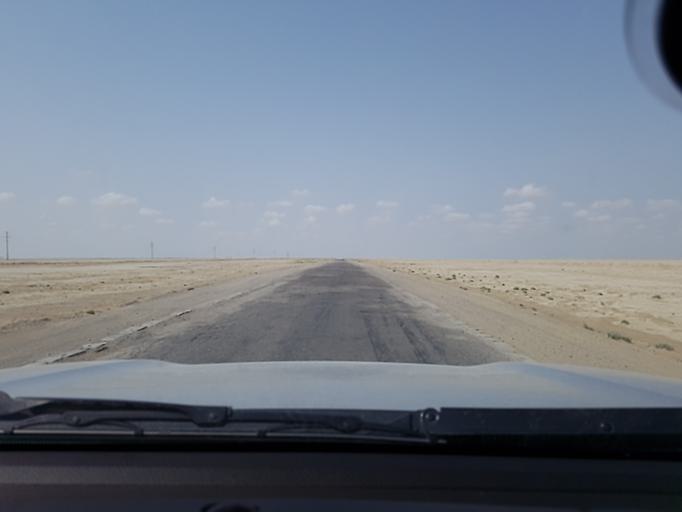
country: TM
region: Balkan
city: Gumdag
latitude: 38.6440
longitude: 54.3785
